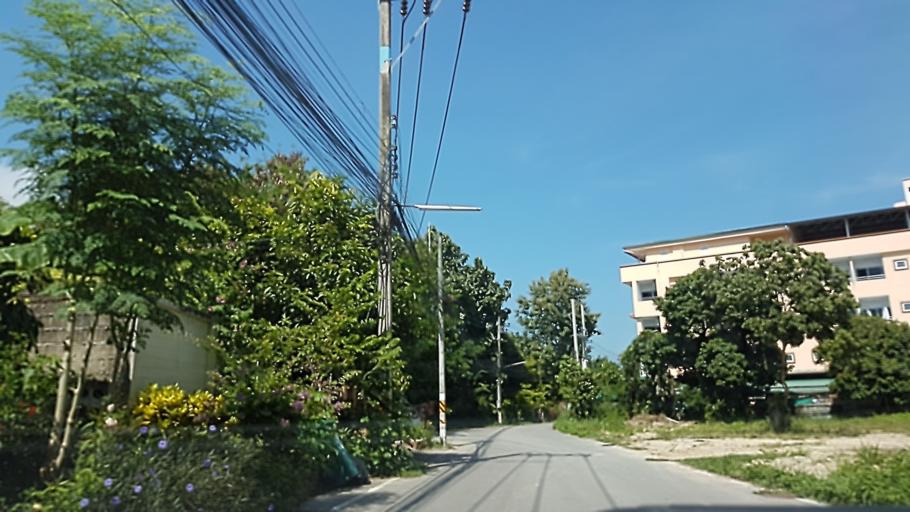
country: TH
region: Chiang Mai
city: Chiang Mai
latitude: 18.8208
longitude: 98.9571
